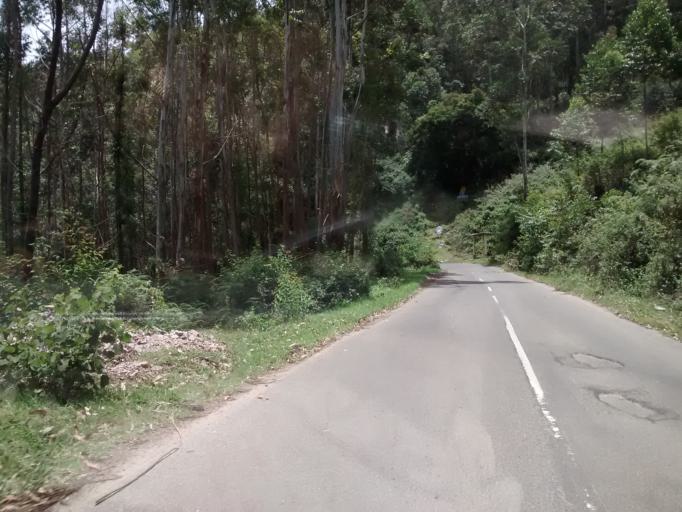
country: IN
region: Kerala
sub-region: Idukki
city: Munnar
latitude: 10.1366
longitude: 77.1833
